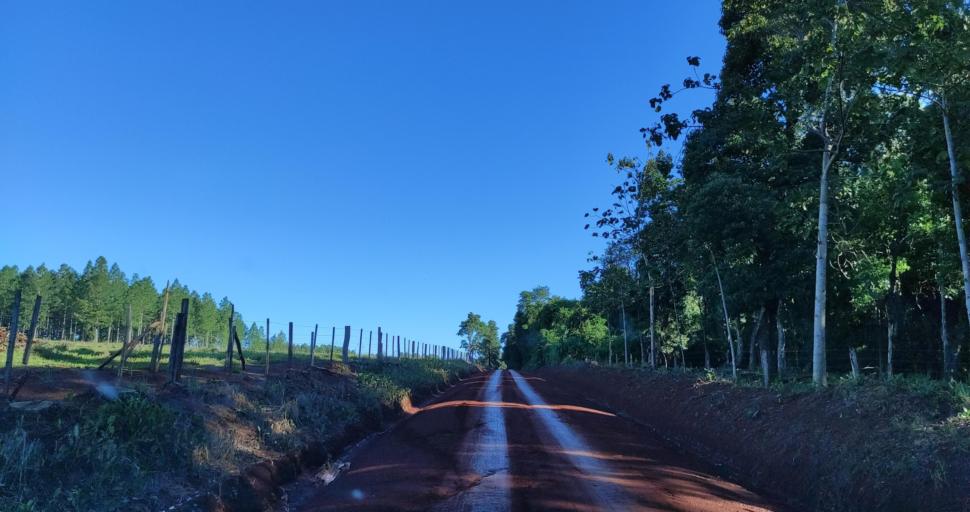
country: AR
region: Misiones
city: Puerto Rico
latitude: -26.8372
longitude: -55.0123
